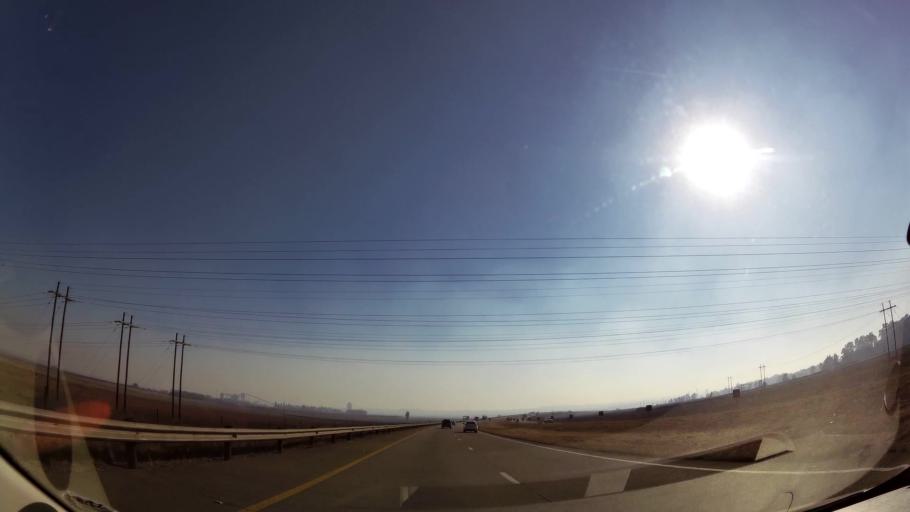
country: ZA
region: Mpumalanga
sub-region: Nkangala District Municipality
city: Witbank
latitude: -25.9519
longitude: 29.1969
